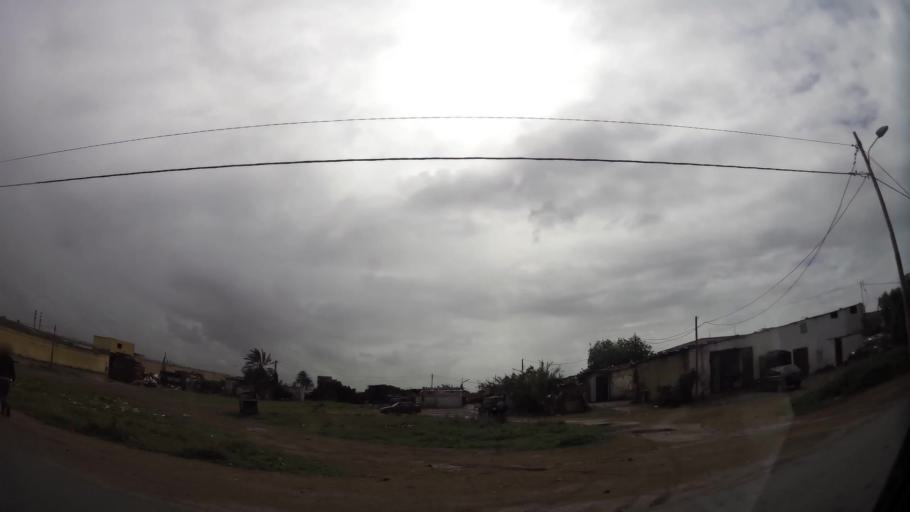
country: MA
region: Grand Casablanca
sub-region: Mediouna
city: Tit Mellil
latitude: 33.6396
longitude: -7.4750
